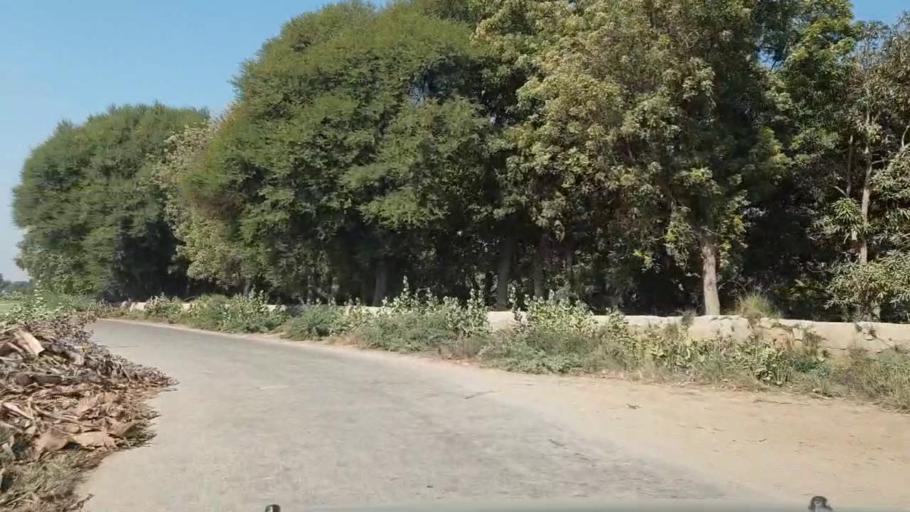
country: PK
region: Sindh
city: Matiari
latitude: 25.6194
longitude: 68.5941
